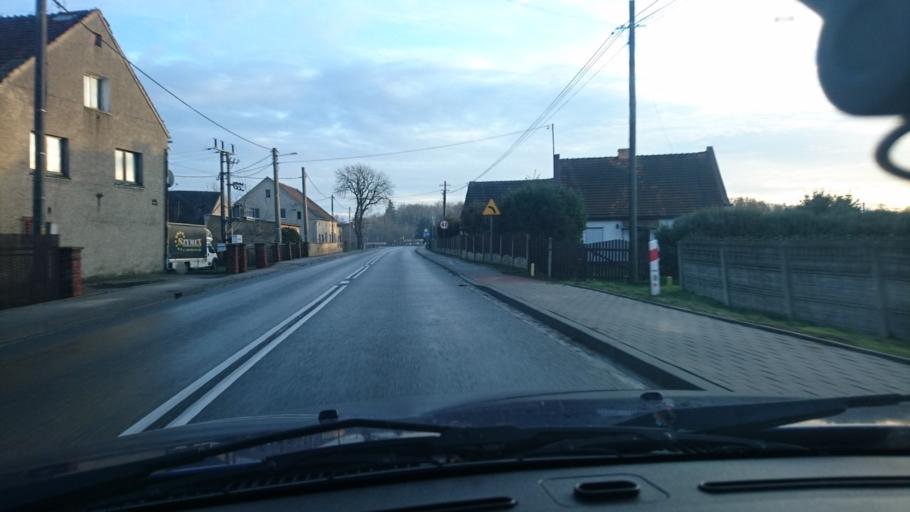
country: PL
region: Greater Poland Voivodeship
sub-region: Powiat kepinski
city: Opatow
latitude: 51.1668
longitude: 18.1471
